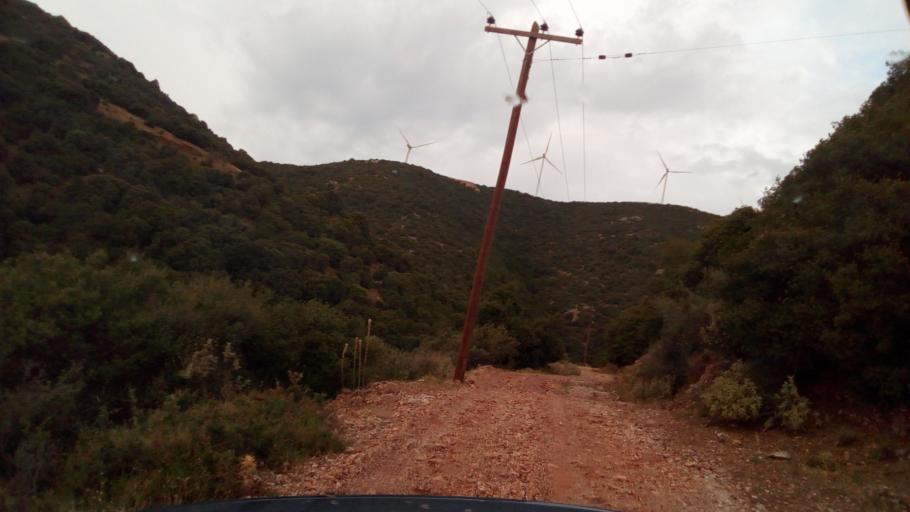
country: GR
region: West Greece
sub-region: Nomos Achaias
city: Kamarai
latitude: 38.4134
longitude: 22.0522
